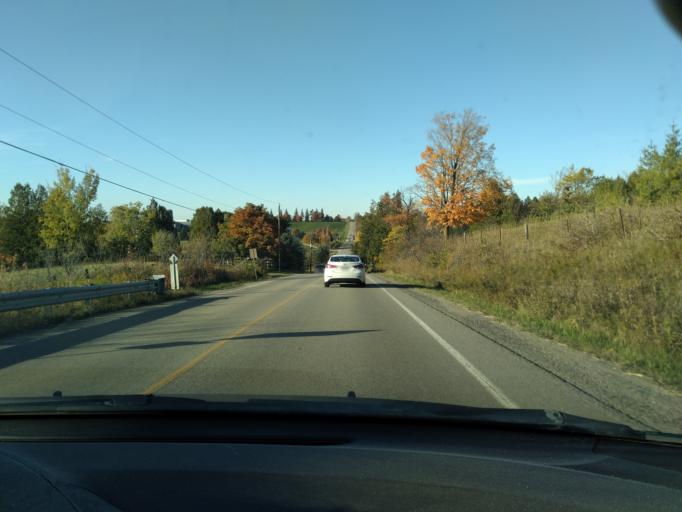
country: CA
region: Ontario
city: Bradford West Gwillimbury
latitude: 43.9833
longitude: -79.7235
